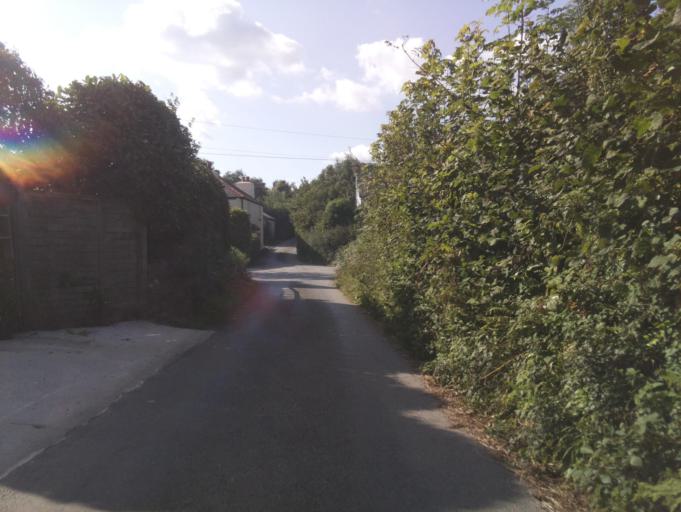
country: GB
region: England
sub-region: Devon
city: Buckfastleigh
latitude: 50.4364
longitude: -3.7793
